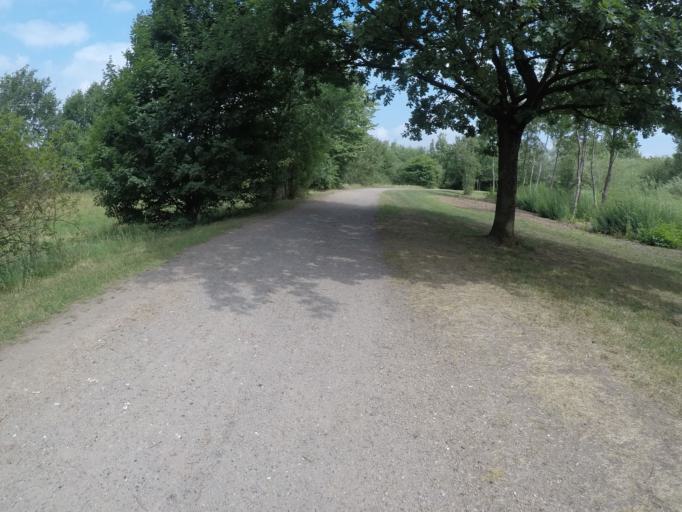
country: DE
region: Hamburg
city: Eidelstedt
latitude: 53.5788
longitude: 9.8735
